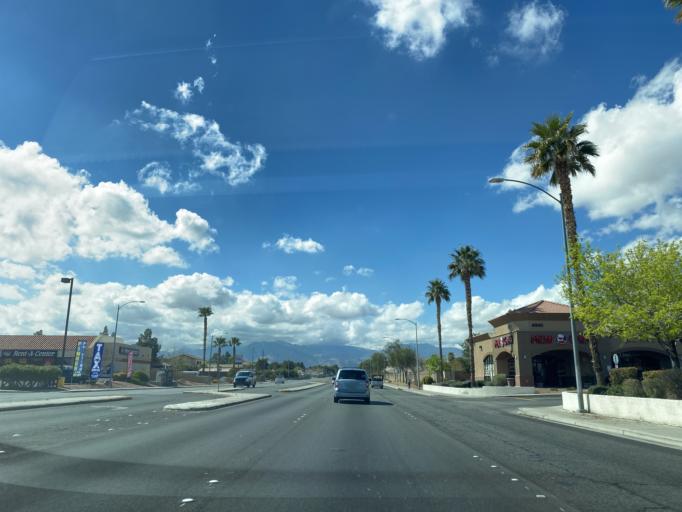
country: US
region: Nevada
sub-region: Clark County
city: Las Vegas
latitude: 36.2389
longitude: -115.2093
